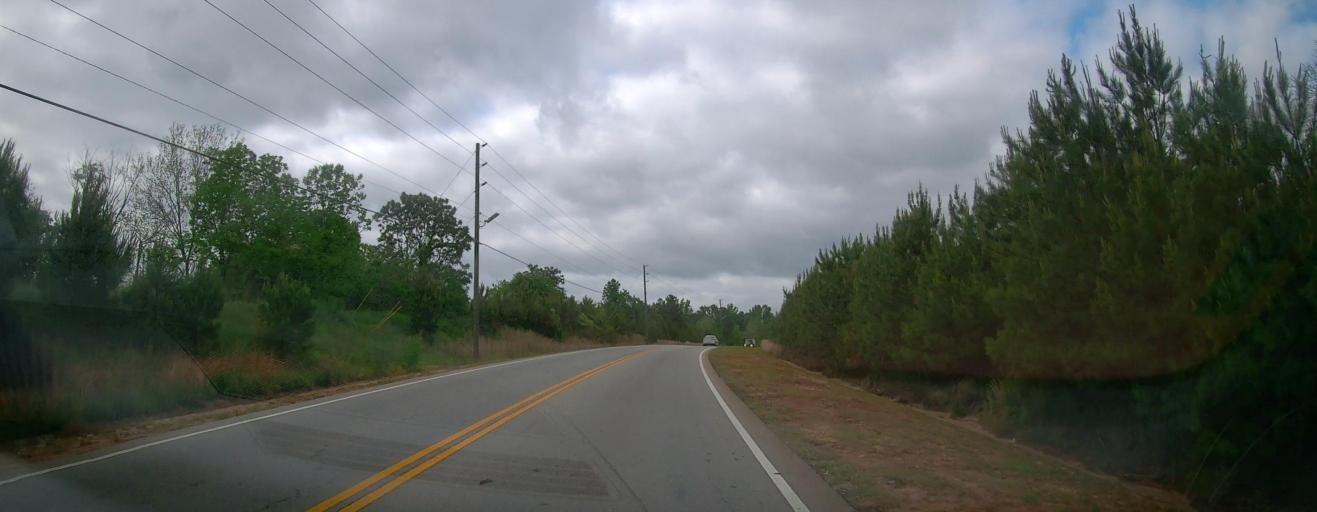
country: US
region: Georgia
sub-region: Walton County
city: Monroe
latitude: 33.8086
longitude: -83.7357
